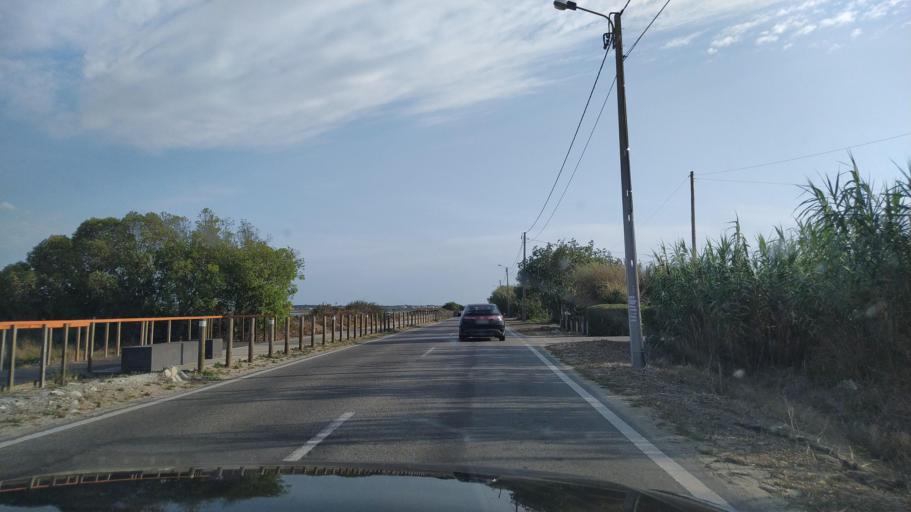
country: PT
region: Aveiro
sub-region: Ilhavo
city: Gafanha da Encarnacao
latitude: 40.5881
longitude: -8.7522
